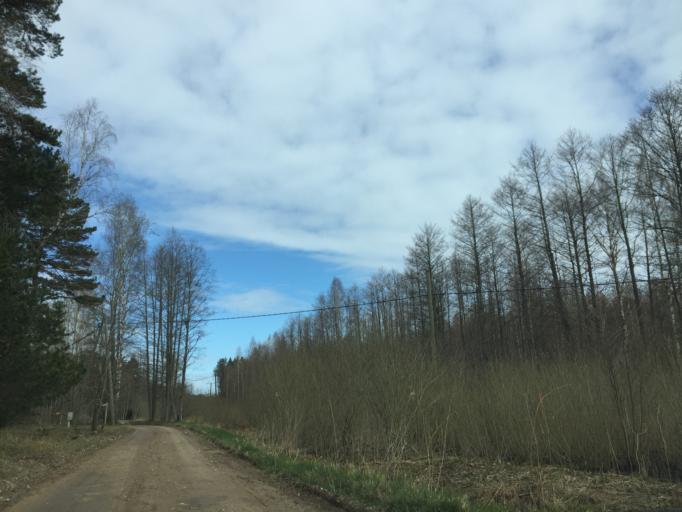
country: LV
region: Salacgrivas
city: Salacgriva
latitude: 57.5341
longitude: 24.3742
